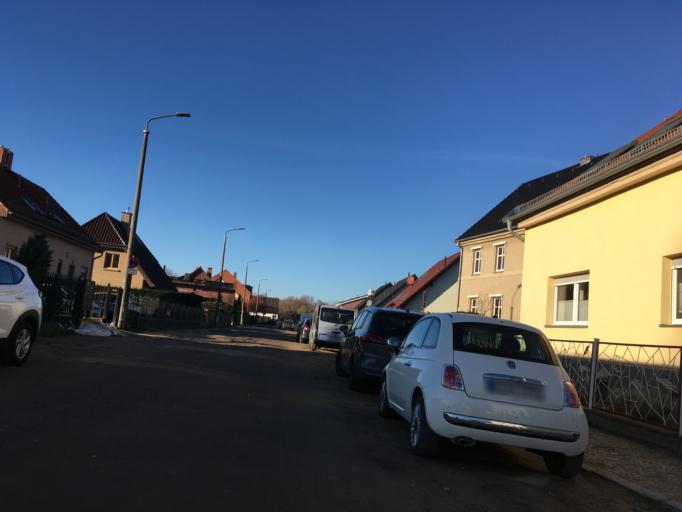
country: DE
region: Berlin
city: Rosenthal
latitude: 52.6032
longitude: 13.3798
